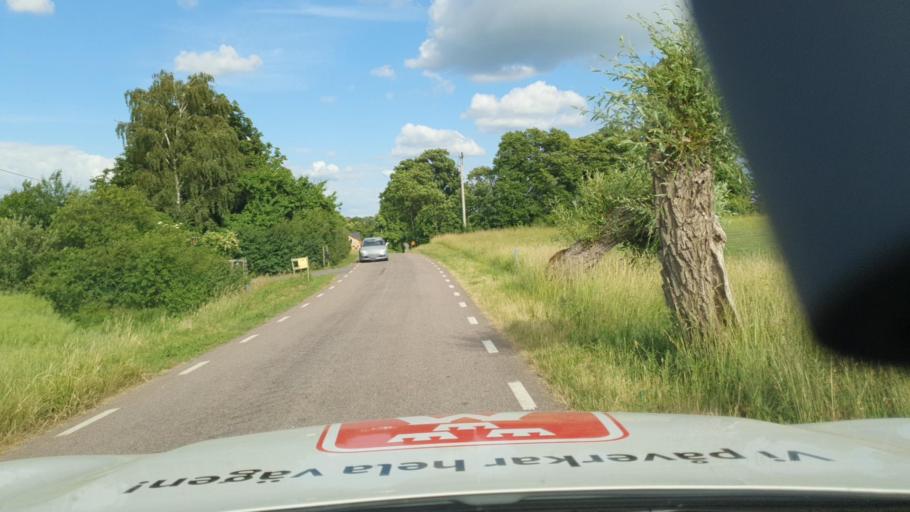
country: SE
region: Skane
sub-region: Skurups Kommun
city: Rydsgard
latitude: 55.4497
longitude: 13.5865
